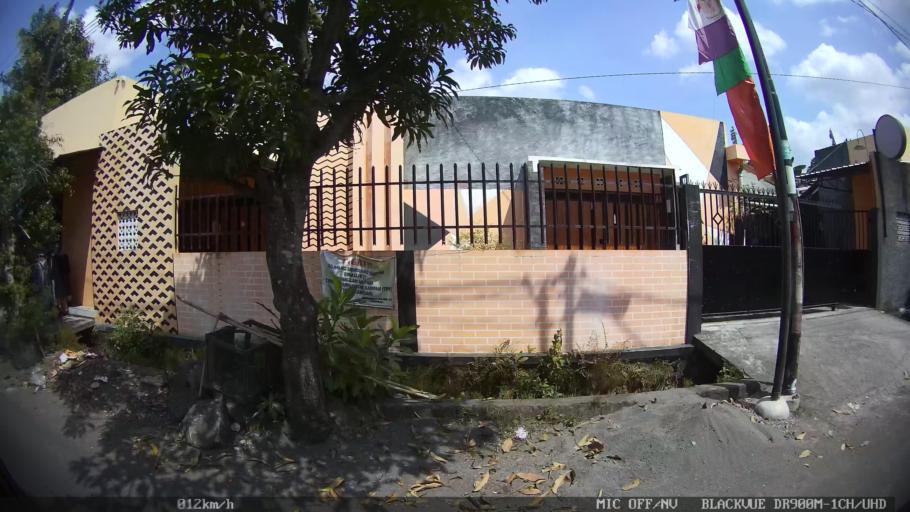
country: ID
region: Daerah Istimewa Yogyakarta
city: Sewon
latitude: -7.8314
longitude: 110.3850
